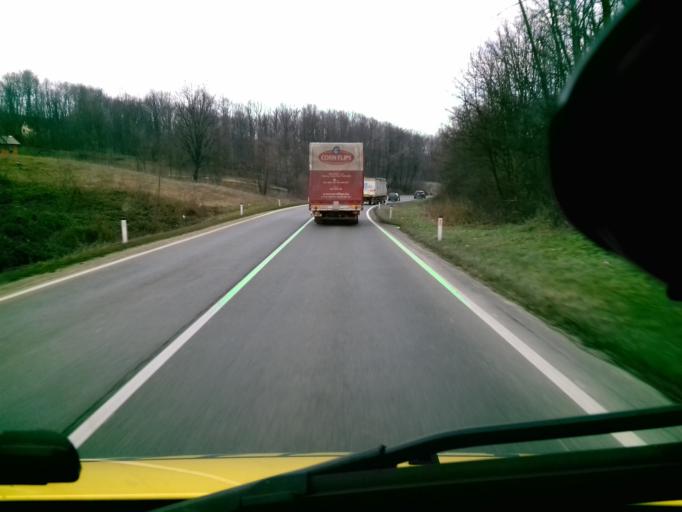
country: BA
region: Federation of Bosnia and Herzegovina
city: Lijesnica
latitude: 44.4664
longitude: 18.0662
